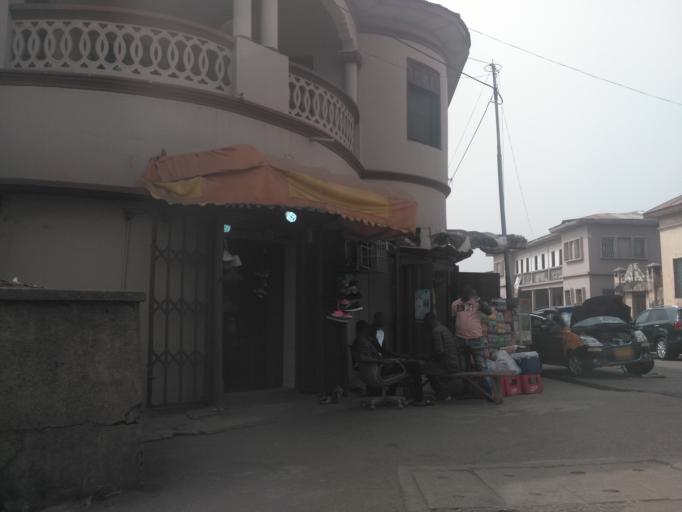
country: GH
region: Ashanti
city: Tafo
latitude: 6.7115
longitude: -1.6166
